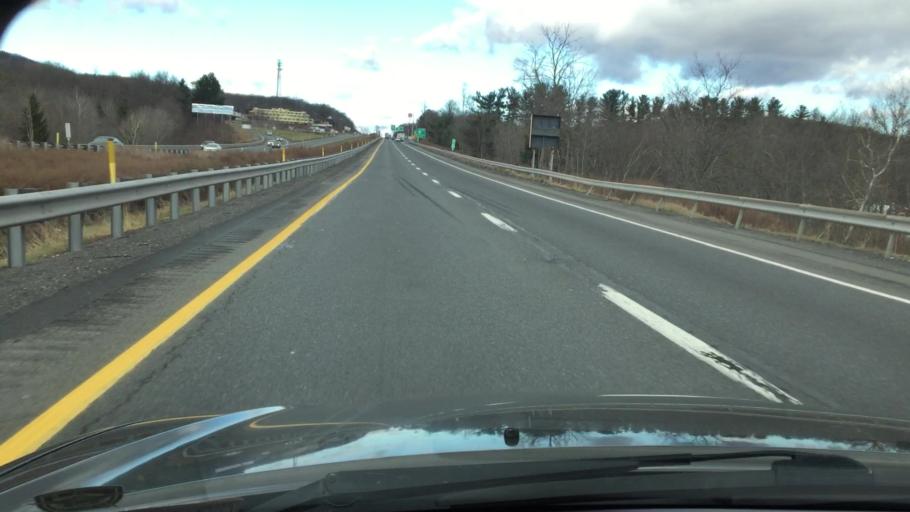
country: US
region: Pennsylvania
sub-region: Monroe County
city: Tannersville
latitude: 41.0337
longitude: -75.3106
